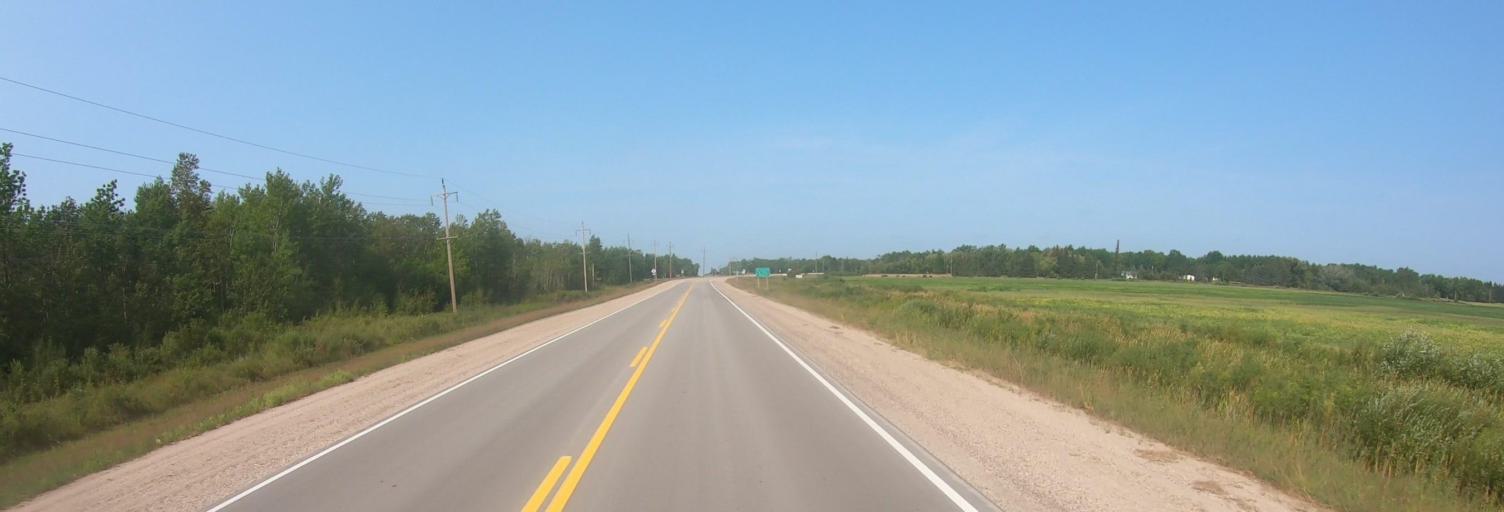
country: US
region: Minnesota
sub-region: Roseau County
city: Roseau
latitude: 49.0896
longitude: -95.9736
